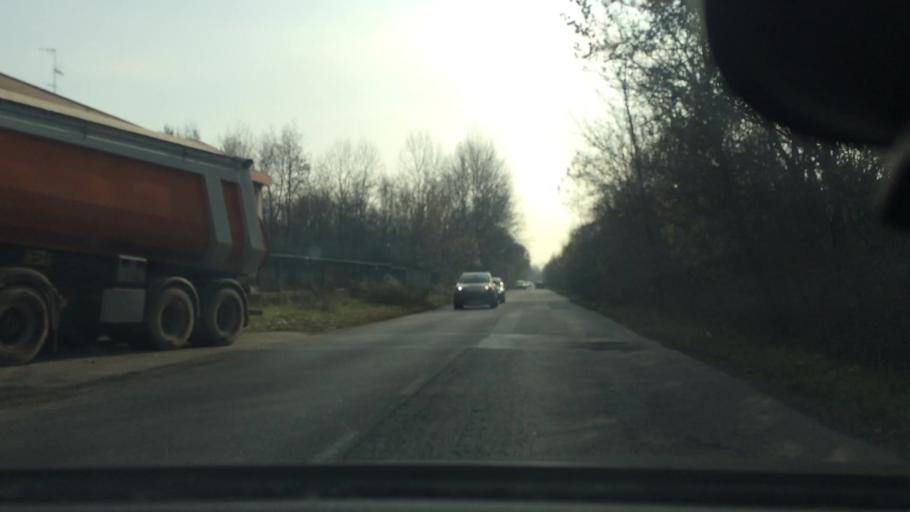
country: IT
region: Lombardy
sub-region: Provincia di Monza e Brianza
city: Villaggio del Sole
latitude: 45.6035
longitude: 9.0958
